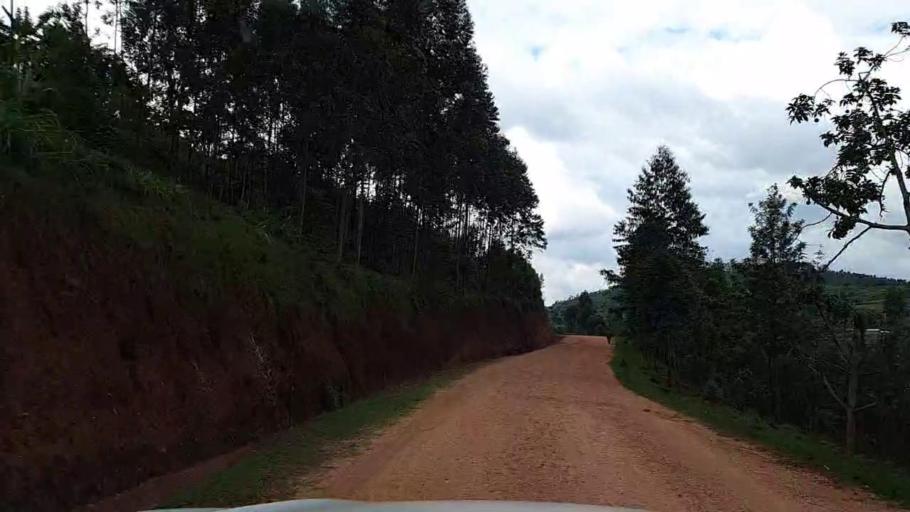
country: RW
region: Southern Province
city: Nyanza
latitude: -2.4109
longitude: 29.6745
